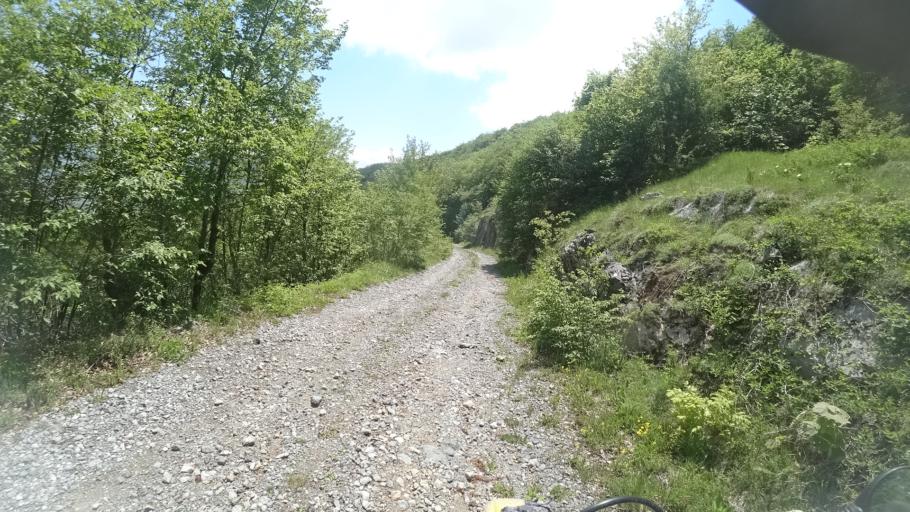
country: HR
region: Zadarska
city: Gracac
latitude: 44.4576
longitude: 15.9103
